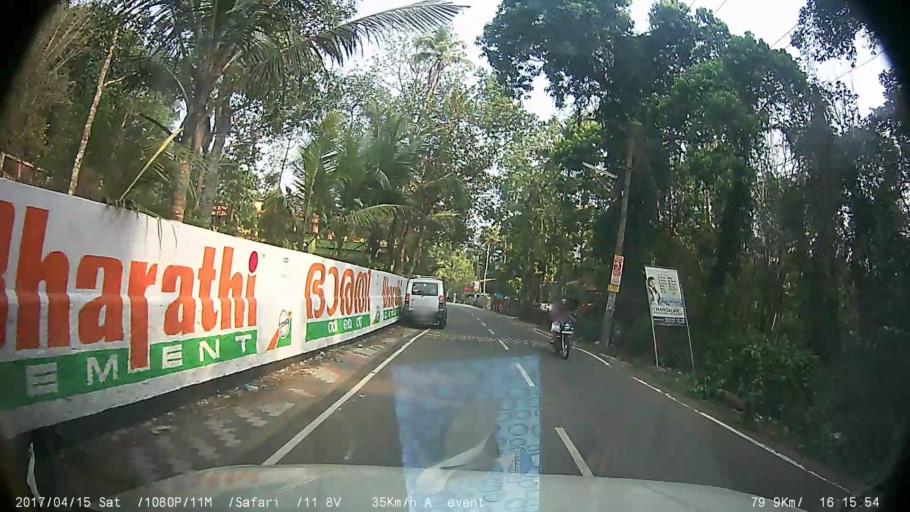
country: IN
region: Kerala
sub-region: Kottayam
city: Kottayam
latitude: 9.6595
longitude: 76.5298
